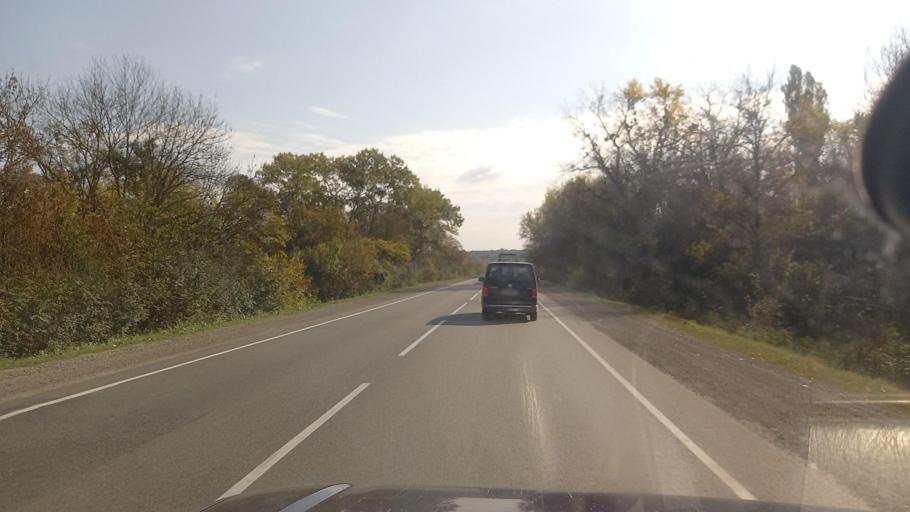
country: RU
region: Krasnodarskiy
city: Abinsk
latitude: 44.8426
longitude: 38.1575
